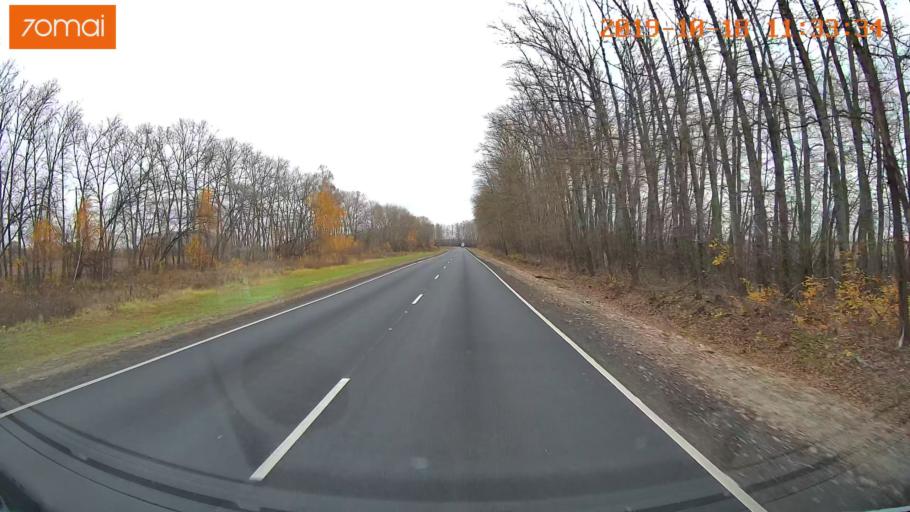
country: RU
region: Rjazan
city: Oktyabr'skiy
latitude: 54.1401
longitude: 38.7434
